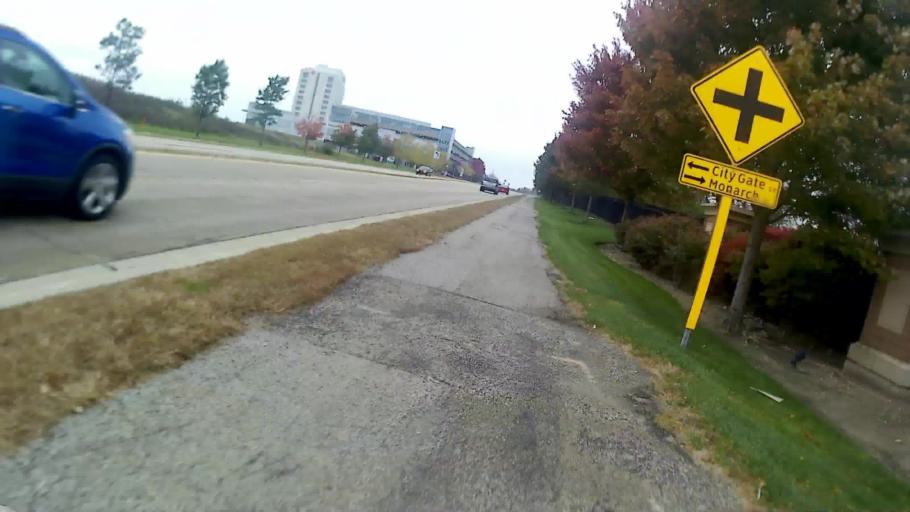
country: US
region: Illinois
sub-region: DuPage County
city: Warrenville
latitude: 41.8089
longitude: -88.1983
